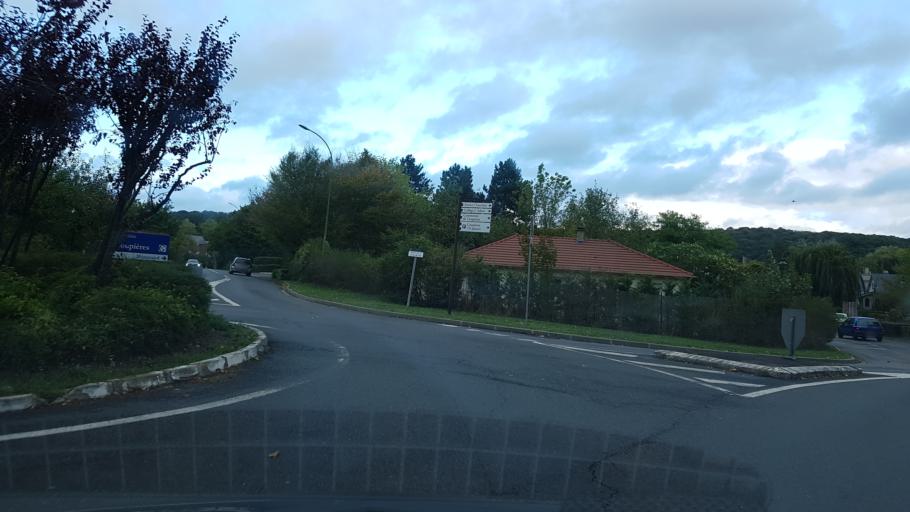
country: FR
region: Ile-de-France
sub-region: Departement de l'Essonne
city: Gif-sur-Yvette
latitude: 48.7003
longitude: 2.1247
